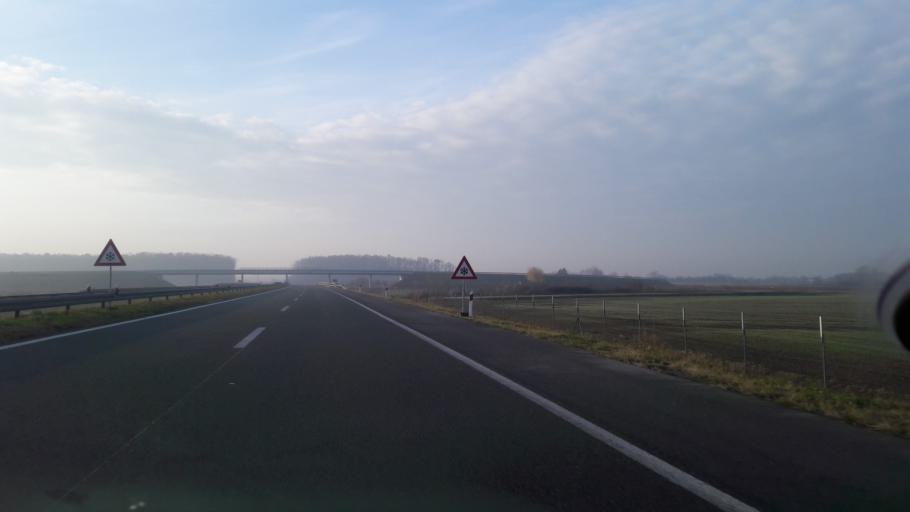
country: HR
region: Osjecko-Baranjska
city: Vuka
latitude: 45.4478
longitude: 18.4635
